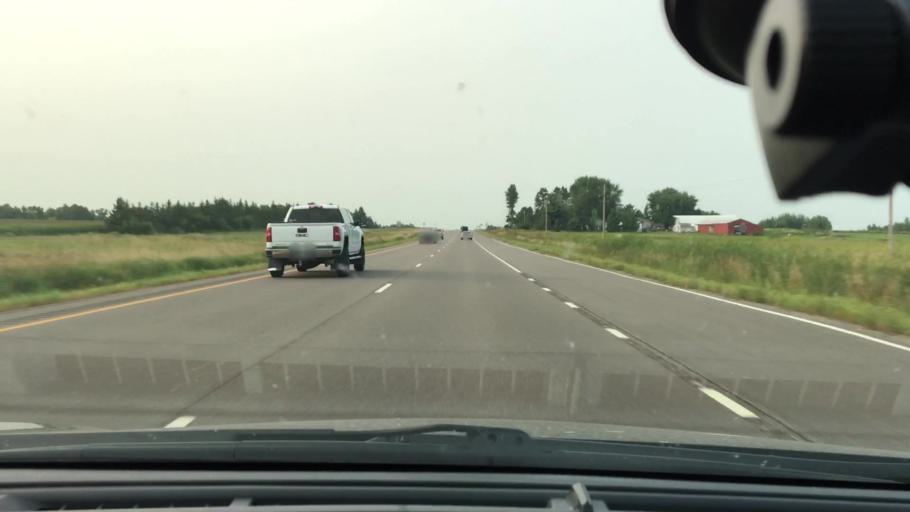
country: US
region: Minnesota
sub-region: Mille Lacs County
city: Milaca
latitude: 45.8444
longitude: -93.6614
